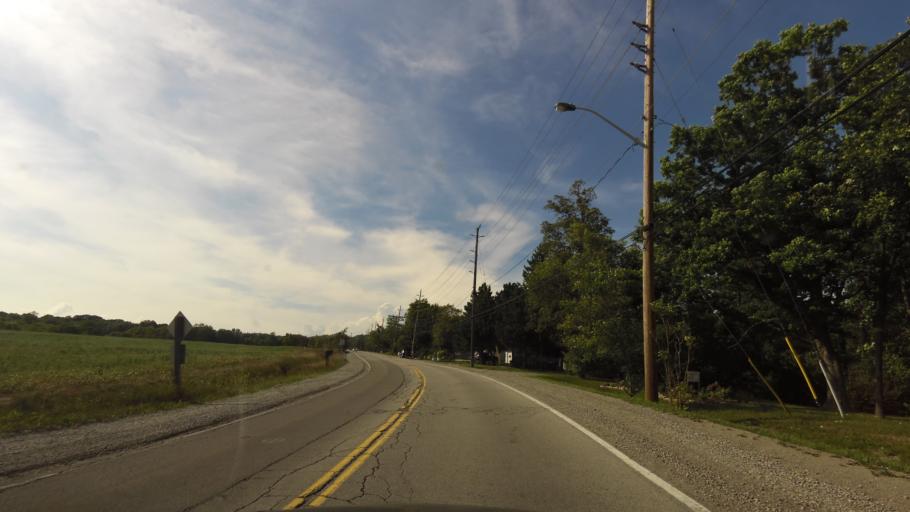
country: CA
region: Ontario
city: Hamilton
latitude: 43.3186
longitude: -79.8693
